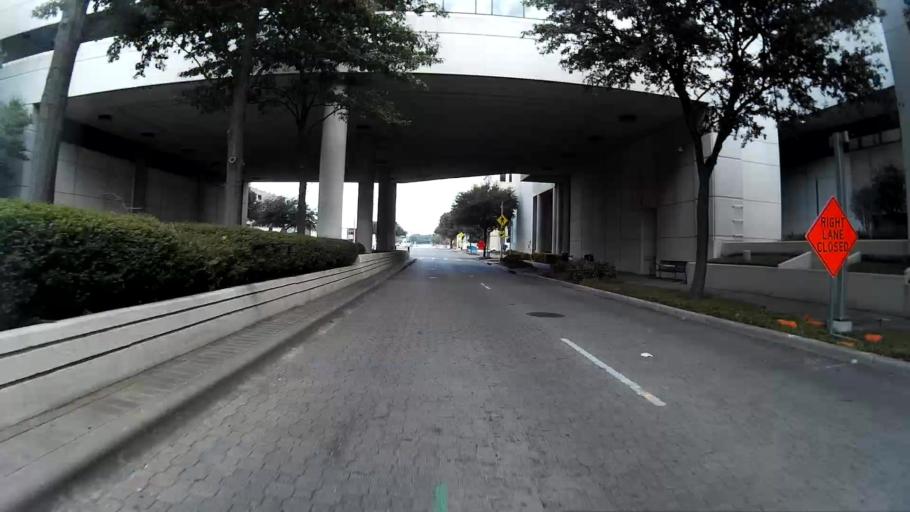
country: US
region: Texas
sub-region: Dallas County
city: Dallas
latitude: 32.7882
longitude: -96.7804
